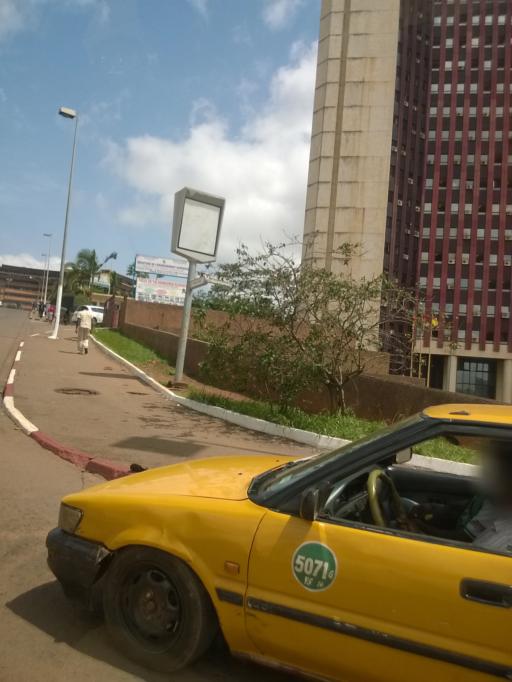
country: CM
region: Centre
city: Yaounde
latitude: 3.8662
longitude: 11.5147
